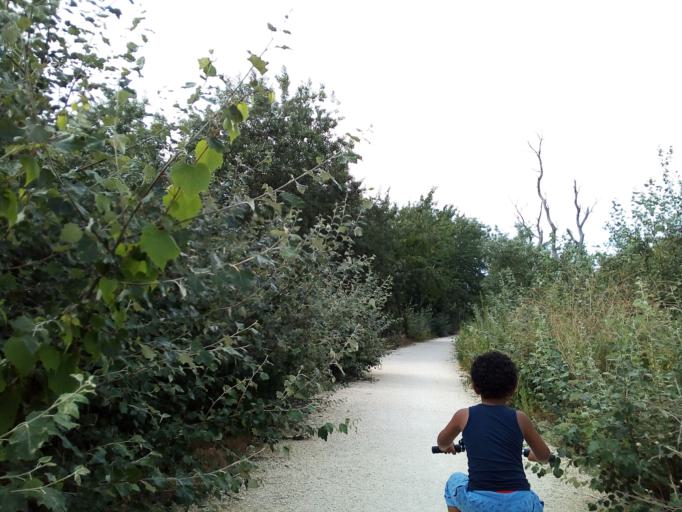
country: FR
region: Poitou-Charentes
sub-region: Departement de la Charente-Maritime
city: Boyard-Ville
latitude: 45.9553
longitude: -1.2450
